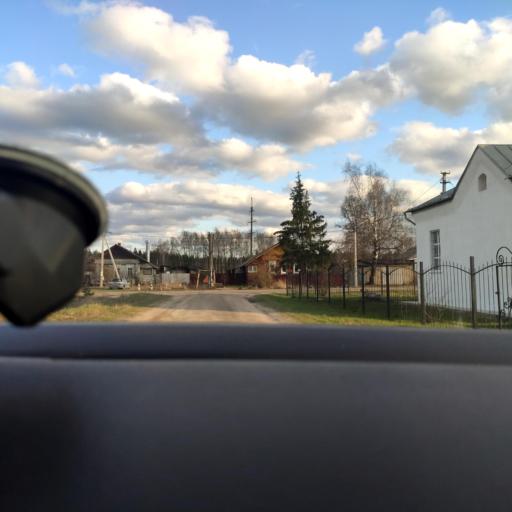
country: RU
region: Moskovskaya
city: Shaturtorf
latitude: 55.4340
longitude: 39.4276
